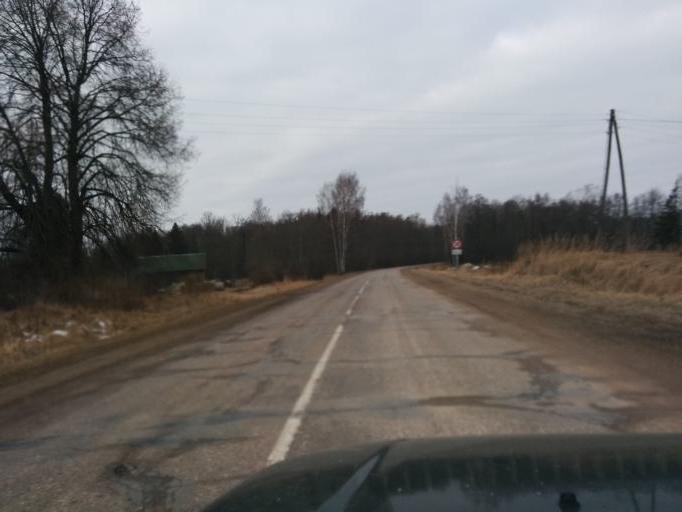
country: LV
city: Tireli
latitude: 56.8357
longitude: 23.5481
